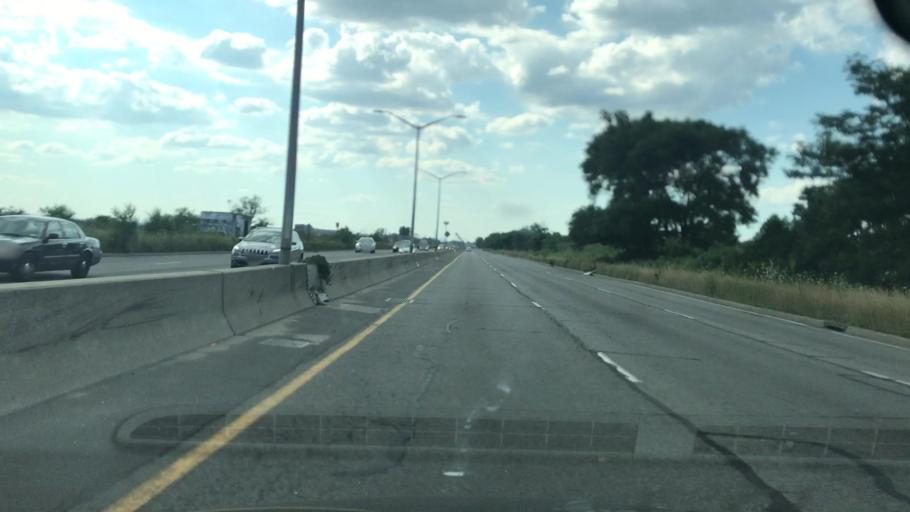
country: US
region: New York
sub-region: Nassau County
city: Inwood
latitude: 40.6460
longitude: -73.7493
